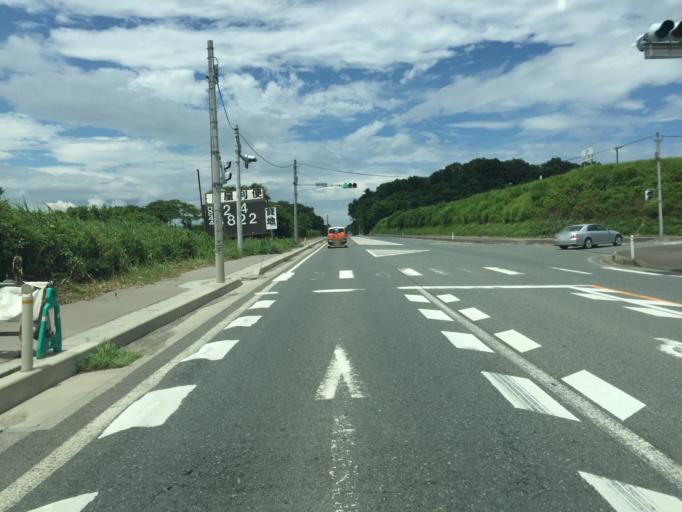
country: JP
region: Fukushima
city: Namie
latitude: 37.7290
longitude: 140.9532
